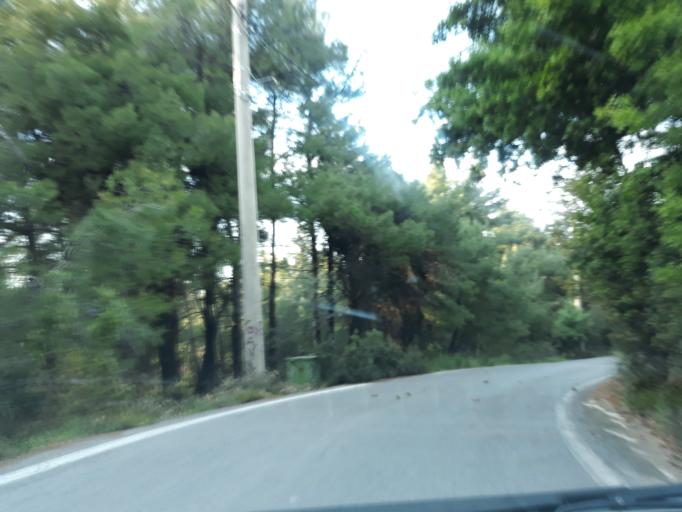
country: GR
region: Attica
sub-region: Nomarchia Anatolikis Attikis
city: Afidnes
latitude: 38.2321
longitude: 23.7875
